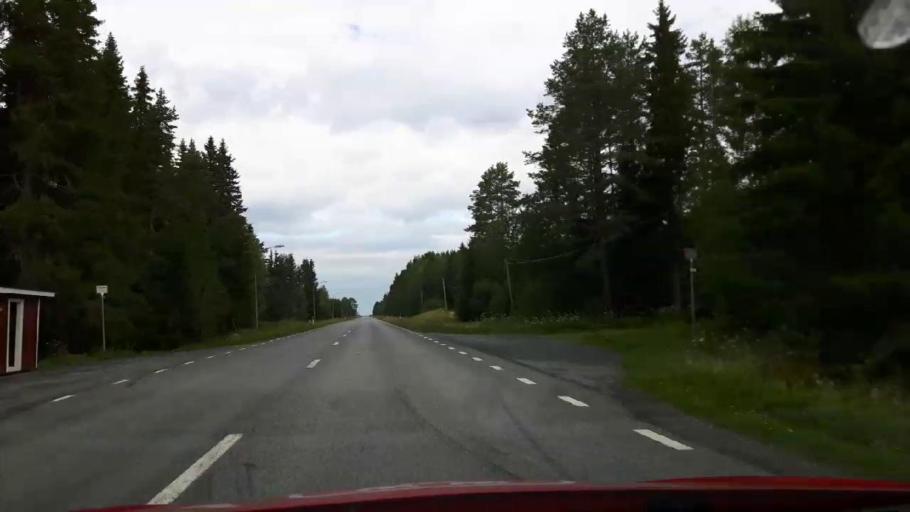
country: SE
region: Jaemtland
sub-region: Stroemsunds Kommun
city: Stroemsund
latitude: 63.5606
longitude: 15.3699
